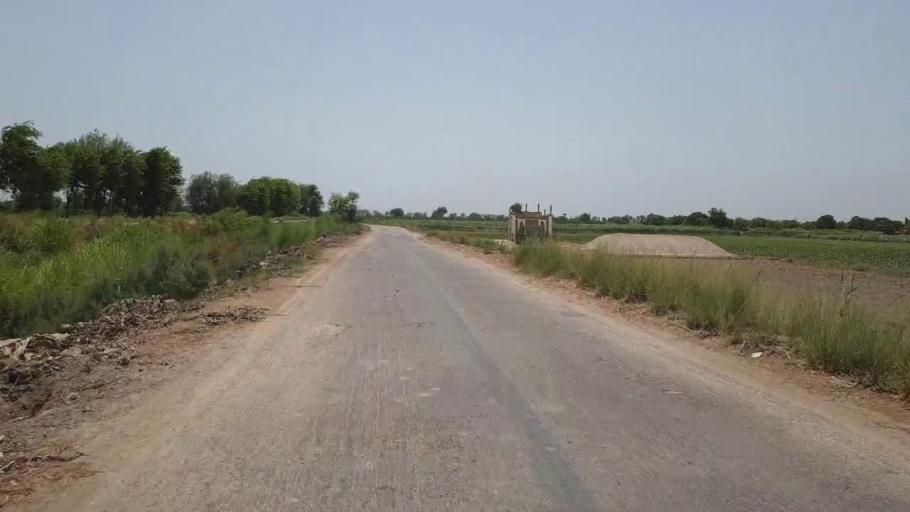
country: PK
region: Sindh
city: Daur
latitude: 26.3854
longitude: 68.1820
